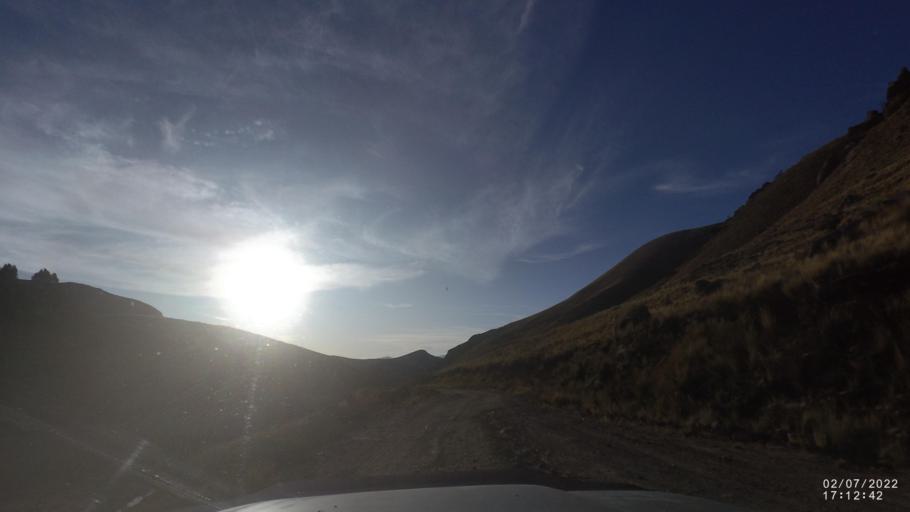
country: BO
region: Cochabamba
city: Irpa Irpa
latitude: -17.8834
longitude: -66.5721
